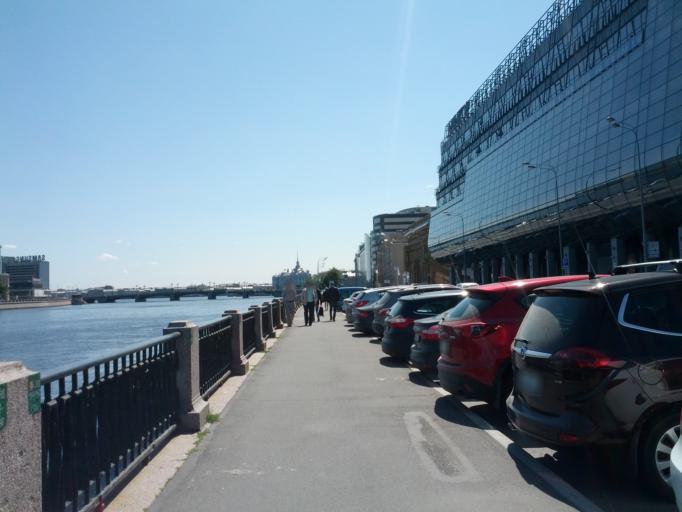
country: RU
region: Leningrad
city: Sampsonievskiy
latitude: 59.9635
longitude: 30.3348
